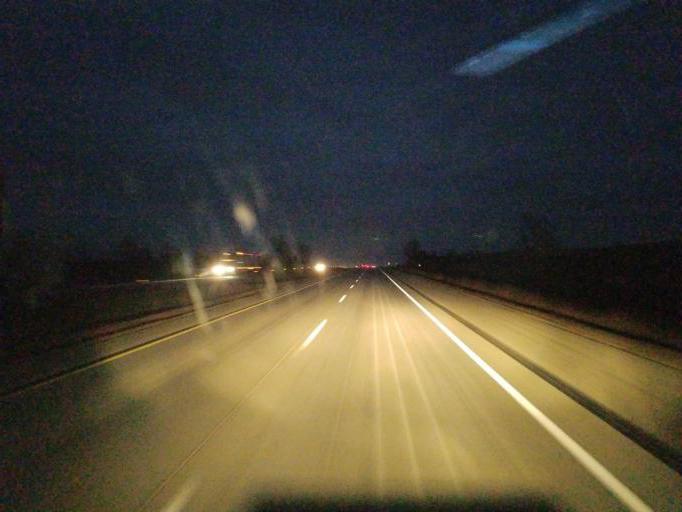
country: US
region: Iowa
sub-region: Guthrie County
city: Stuart
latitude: 41.4960
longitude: -94.4992
